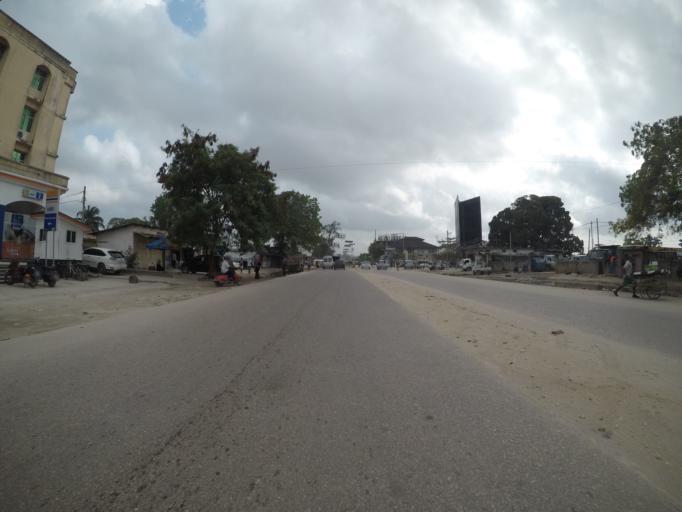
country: TZ
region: Zanzibar Urban/West
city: Zanzibar
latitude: -6.1772
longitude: 39.2224
